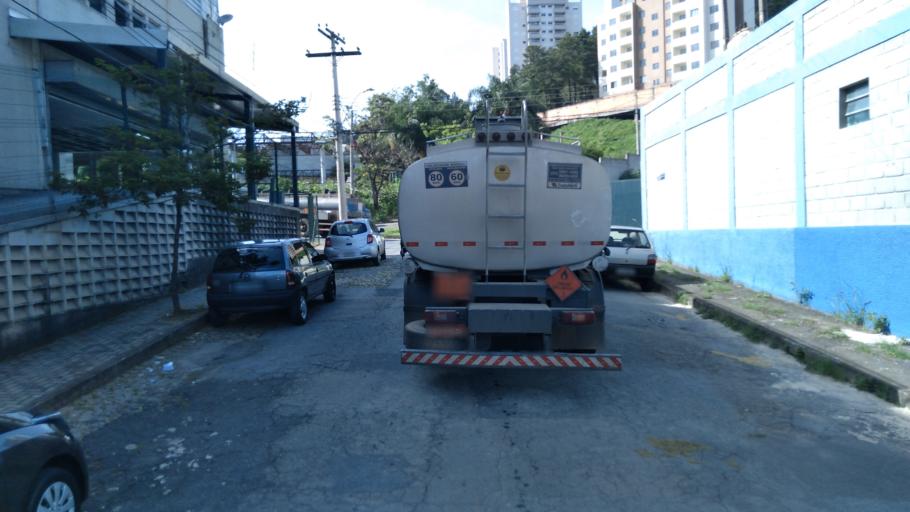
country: BR
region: Minas Gerais
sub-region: Belo Horizonte
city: Belo Horizonte
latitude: -19.8969
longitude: -43.9664
